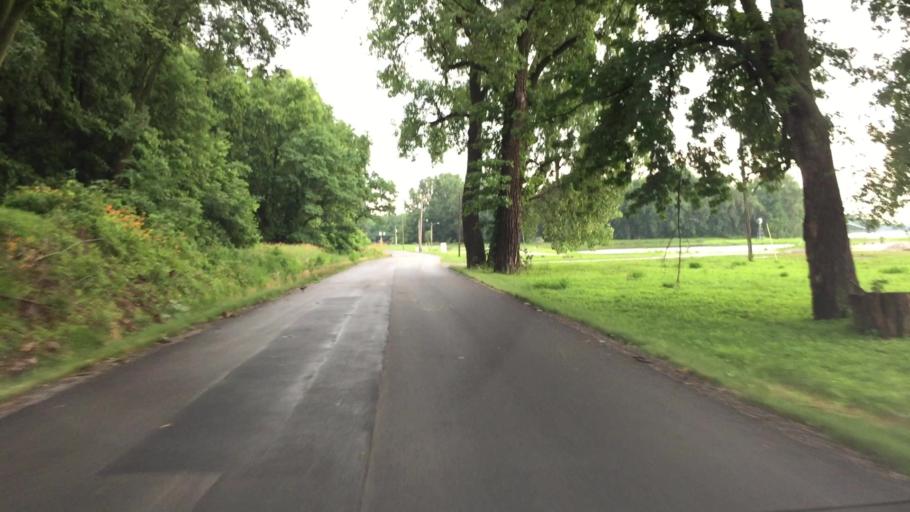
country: US
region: Illinois
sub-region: Hancock County
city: Warsaw
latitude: 40.3553
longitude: -91.4453
